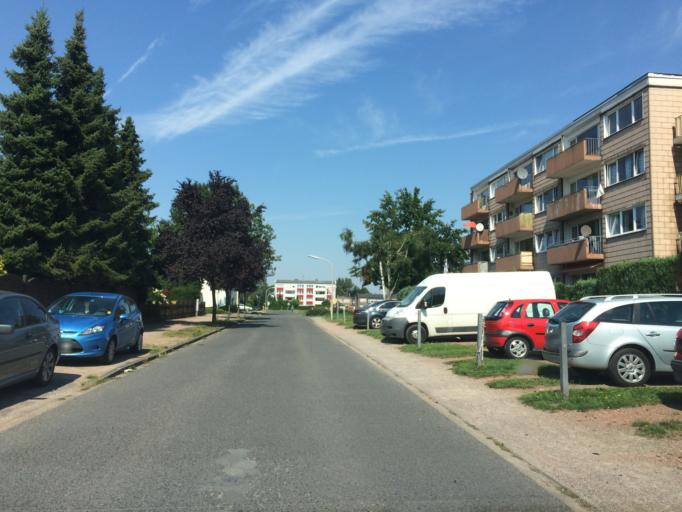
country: DE
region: North Rhine-Westphalia
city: Dorsten
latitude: 51.6704
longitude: 6.9997
